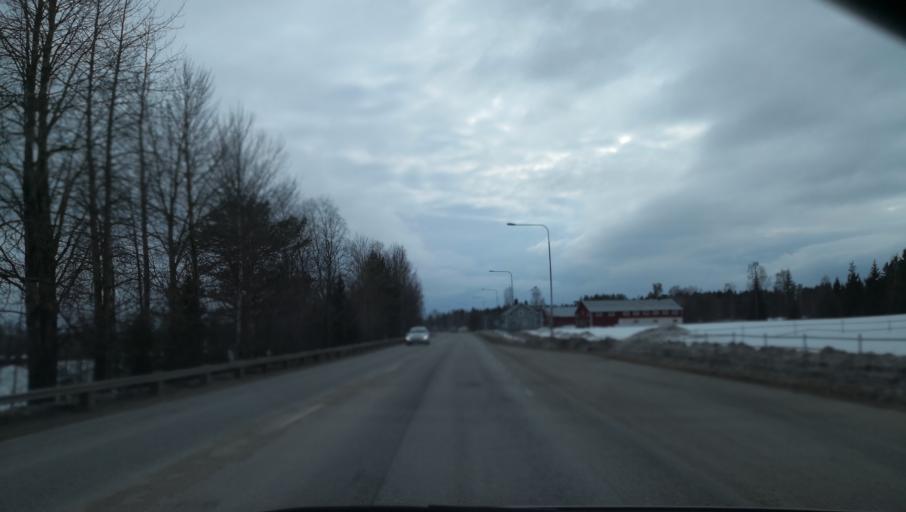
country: SE
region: Vaesterbotten
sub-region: Vannas Kommun
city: Vaennaes
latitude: 63.9169
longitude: 19.7768
